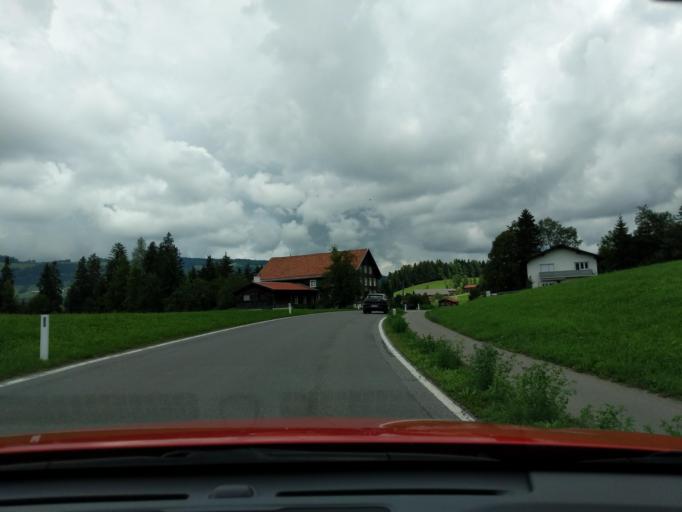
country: AT
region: Vorarlberg
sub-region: Politischer Bezirk Bregenz
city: Krumbach
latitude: 47.4945
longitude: 9.9458
